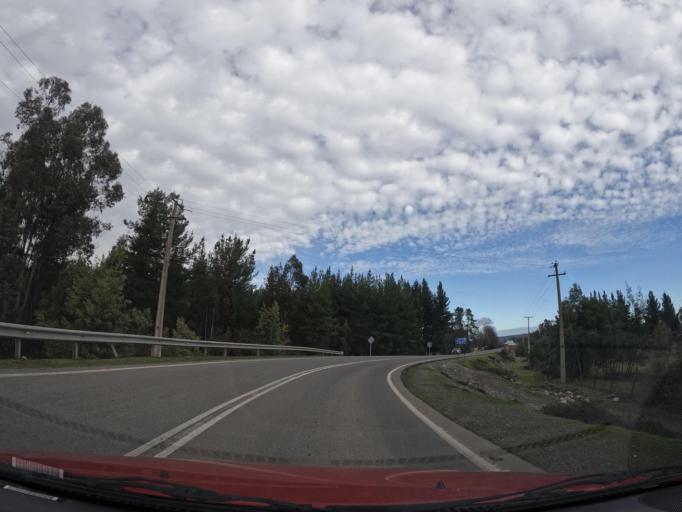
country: CL
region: Maule
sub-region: Provincia de Linares
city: Linares
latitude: -35.9093
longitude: -71.4911
